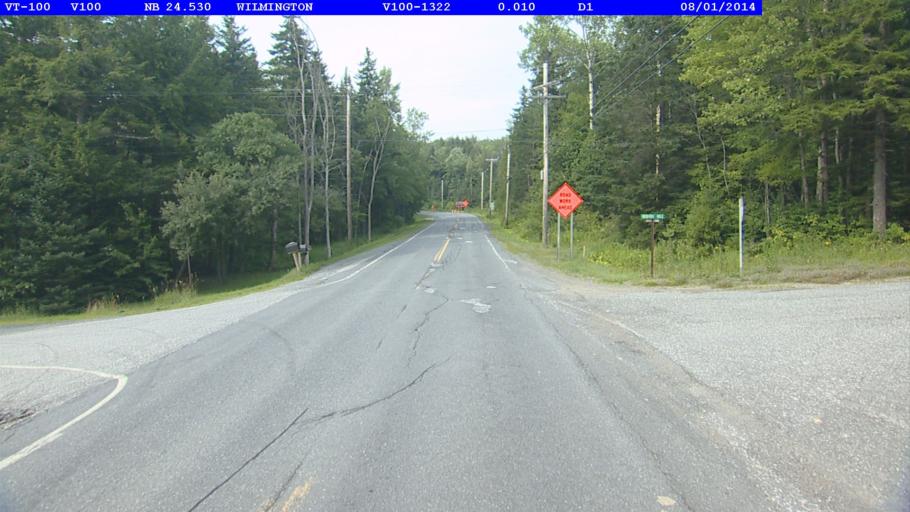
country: US
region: Vermont
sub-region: Windham County
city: Dover
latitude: 42.8281
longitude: -72.8557
